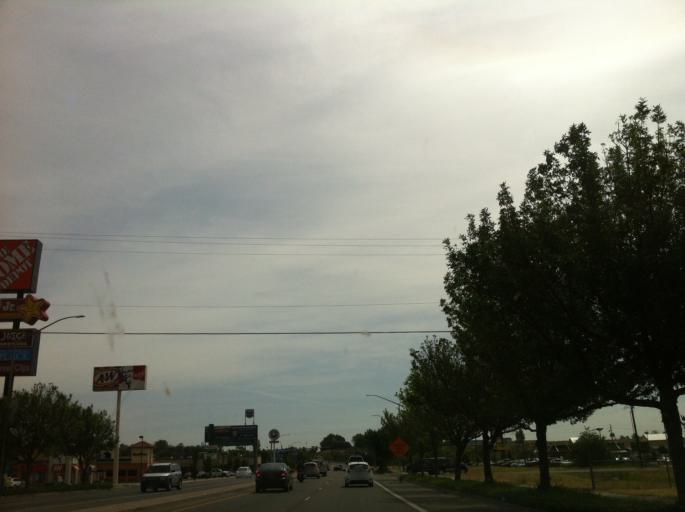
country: US
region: Oregon
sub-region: Malheur County
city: Ontario
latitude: 44.0246
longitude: -116.9454
